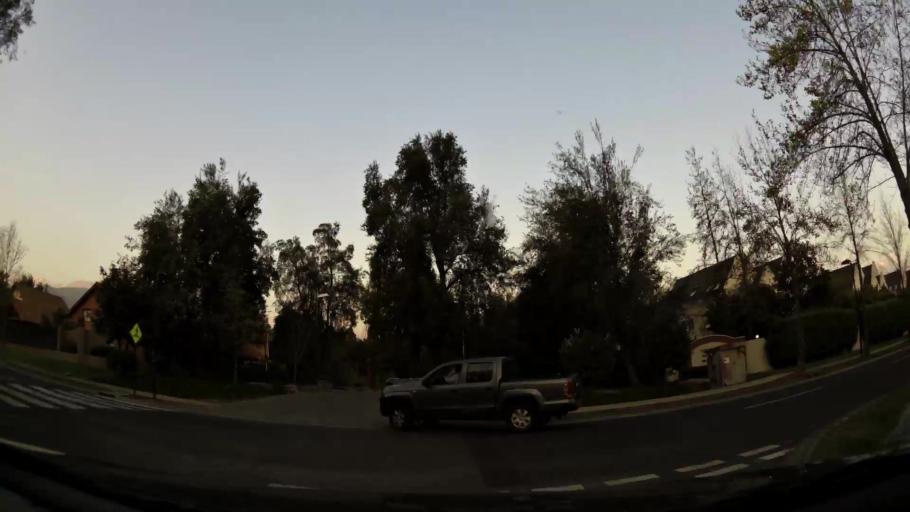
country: CL
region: Santiago Metropolitan
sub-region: Provincia de Chacabuco
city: Chicureo Abajo
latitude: -33.3344
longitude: -70.5521
